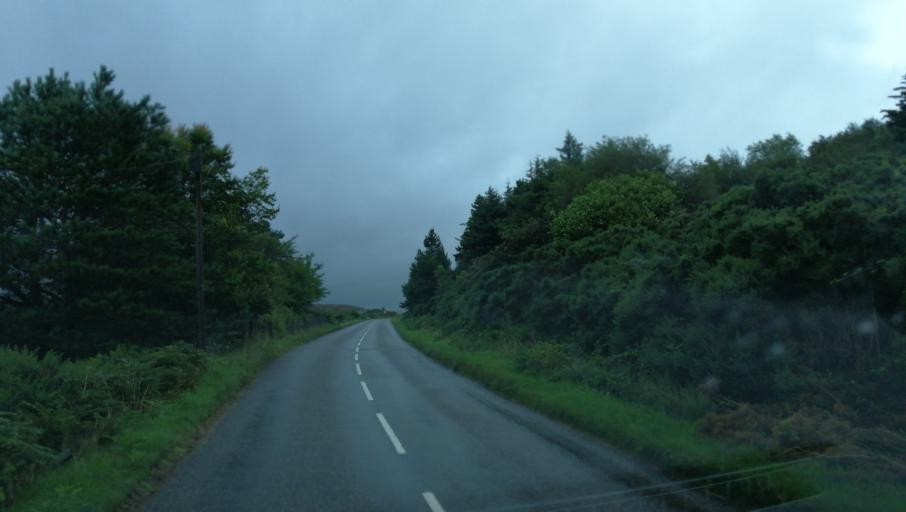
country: GB
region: Scotland
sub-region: Highland
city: Ullapool
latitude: 57.7307
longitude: -5.6904
